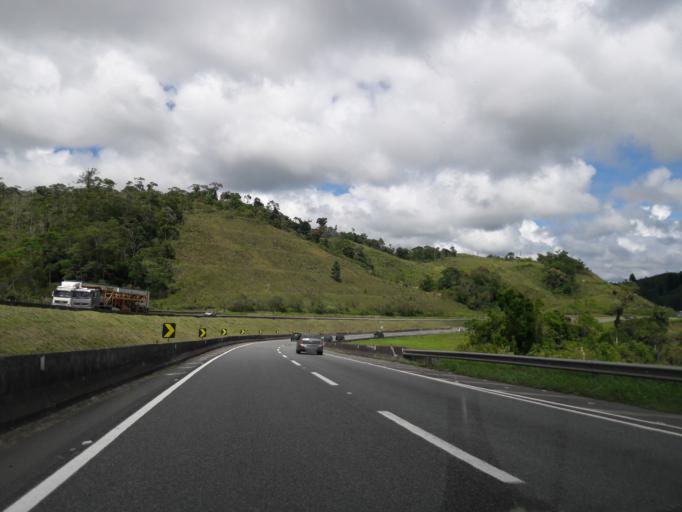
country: BR
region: Parana
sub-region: Antonina
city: Antonina
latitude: -25.0172
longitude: -48.5101
